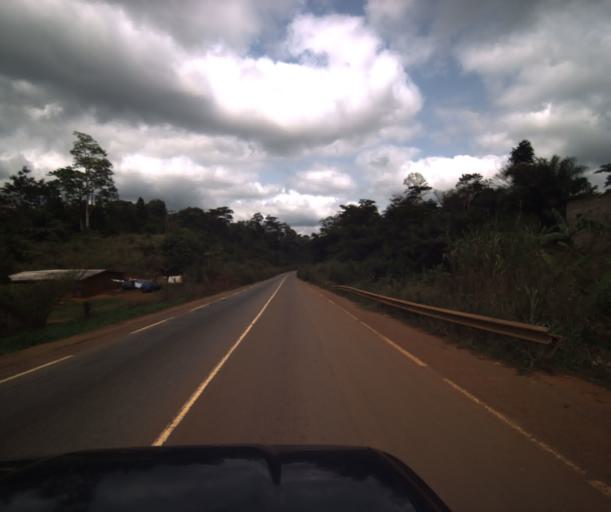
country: CM
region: Centre
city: Mbankomo
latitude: 3.7912
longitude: 11.3957
